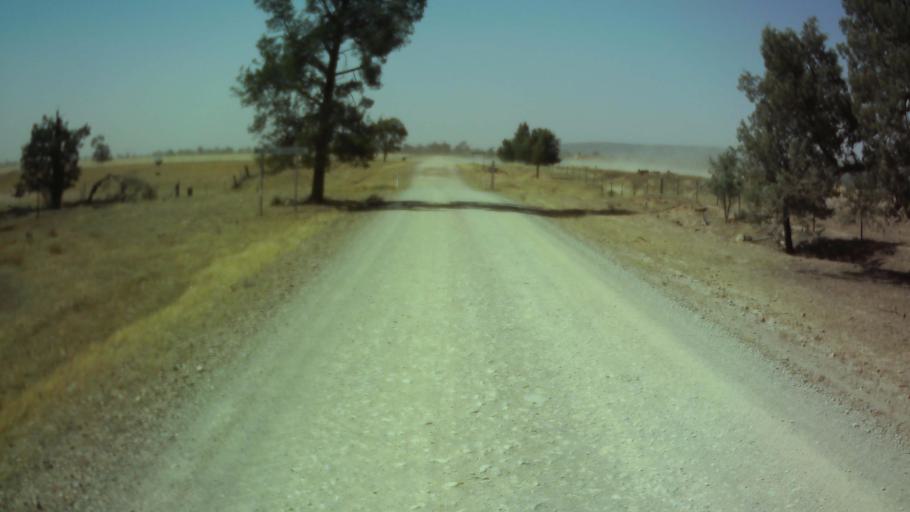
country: AU
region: New South Wales
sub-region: Weddin
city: Grenfell
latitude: -34.0165
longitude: 147.9153
